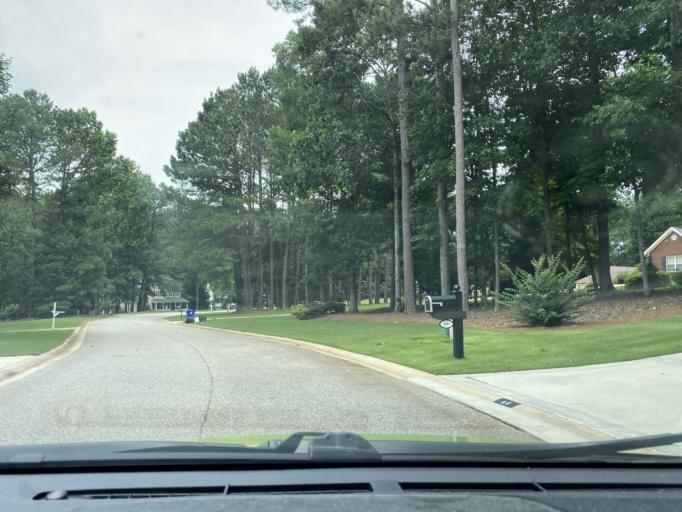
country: US
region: Georgia
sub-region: Fayette County
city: Peachtree City
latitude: 33.4262
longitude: -84.6753
